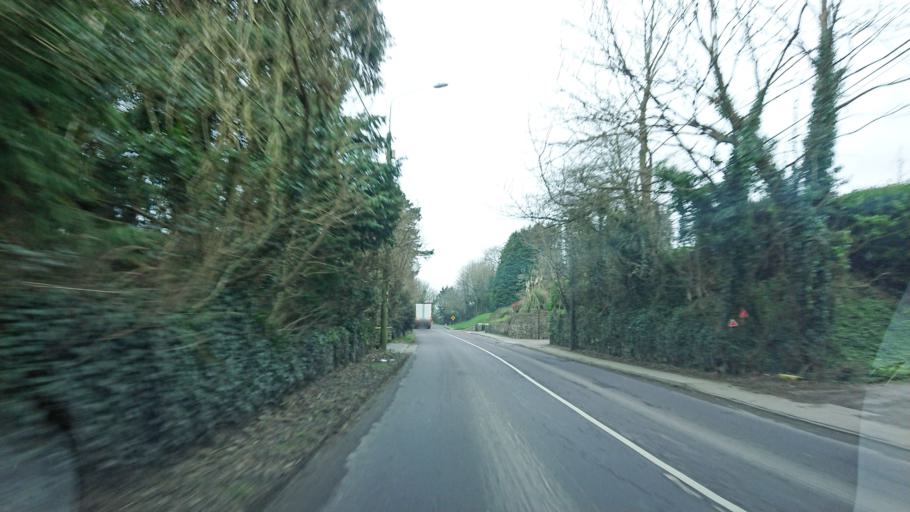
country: IE
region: Munster
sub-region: County Cork
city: Bandon
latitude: 51.7468
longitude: -8.7551
